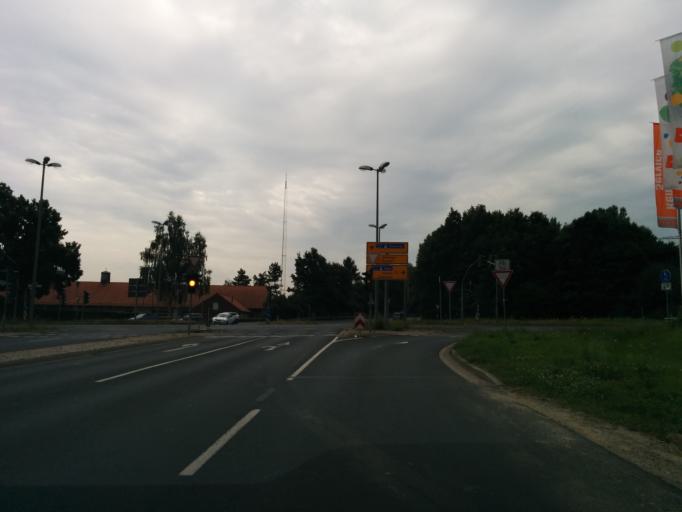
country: DE
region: Lower Saxony
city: Rosdorf
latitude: 51.5261
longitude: 9.8802
